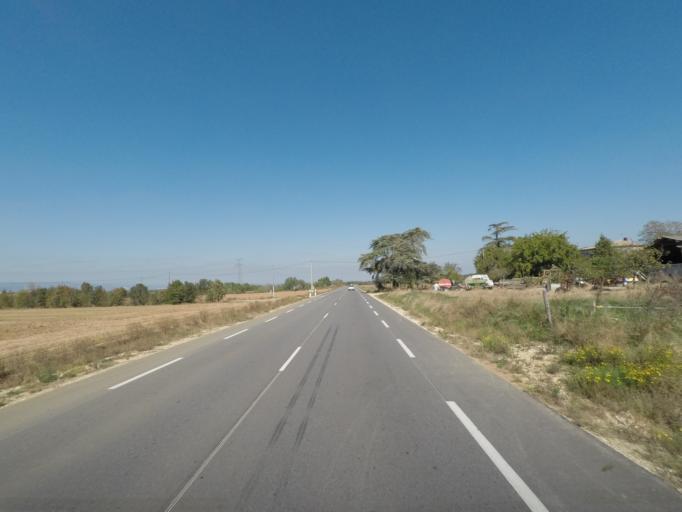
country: FR
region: Rhone-Alpes
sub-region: Departement de la Drome
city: Montmeyran
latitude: 44.8461
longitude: 5.0085
